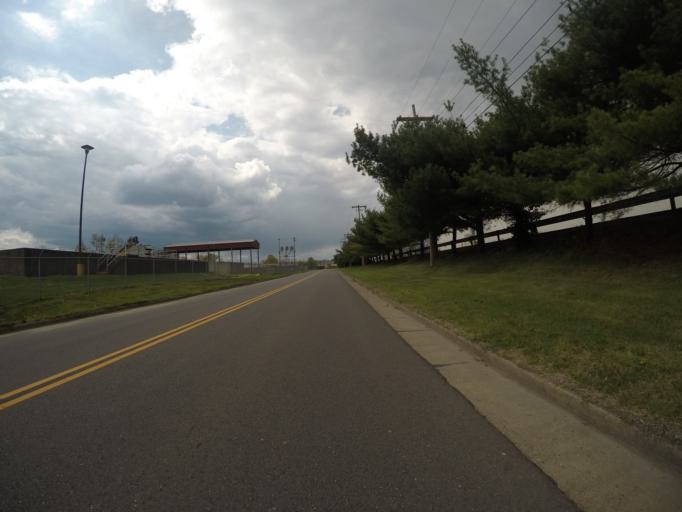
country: US
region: West Virginia
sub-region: Wood County
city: Williamstown
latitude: 39.4095
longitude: -81.4339
